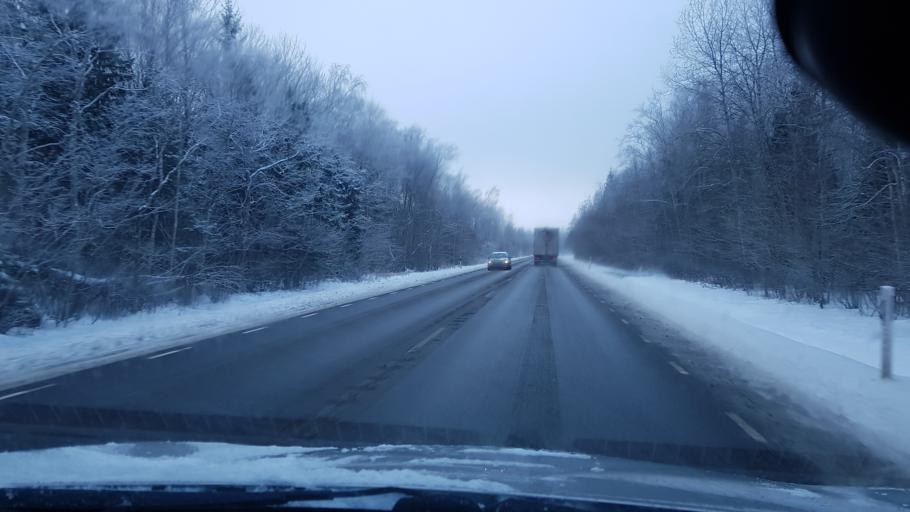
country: EE
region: Harju
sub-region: Paldiski linn
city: Paldiski
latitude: 59.3414
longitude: 24.1624
